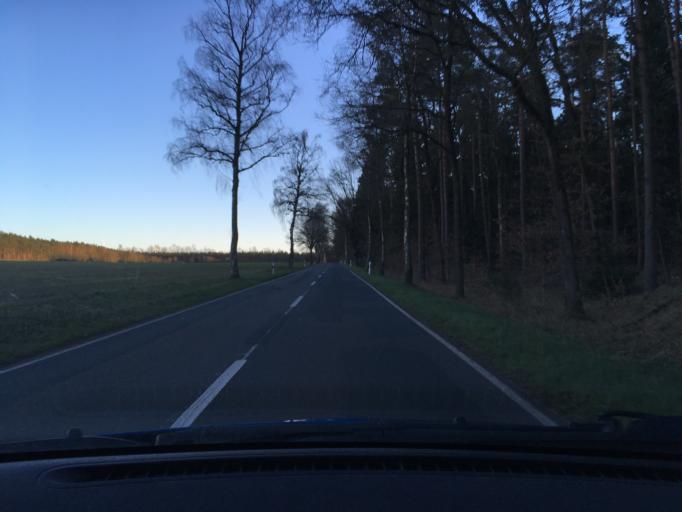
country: DE
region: Lower Saxony
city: Bleckede
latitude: 53.2496
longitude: 10.7466
